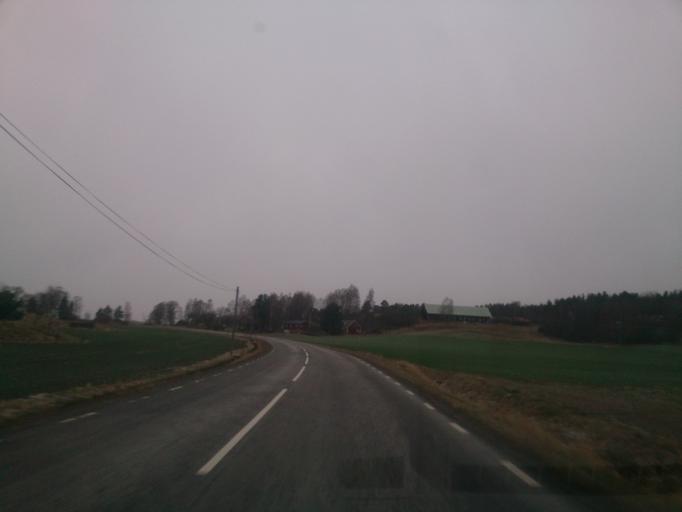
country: SE
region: OEstergoetland
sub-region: Soderkopings Kommun
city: Soederkoeping
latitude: 58.5255
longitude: 16.4473
